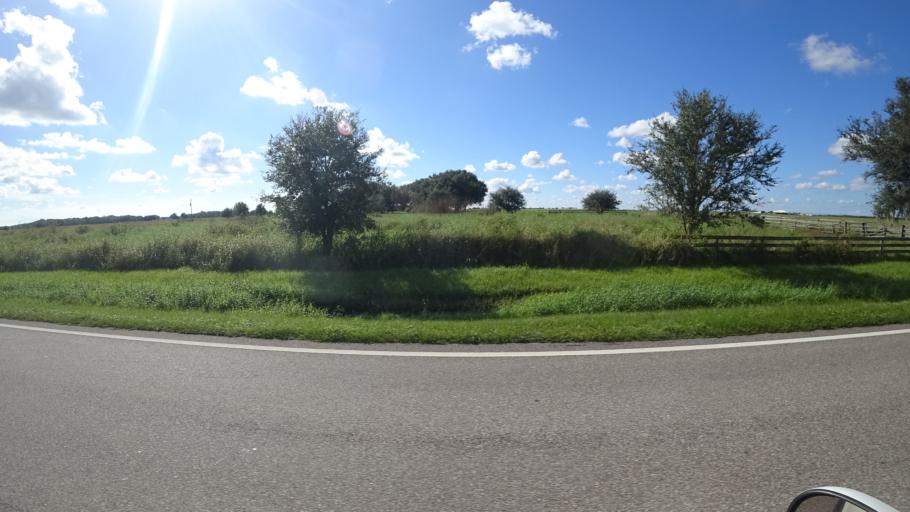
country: US
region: Florida
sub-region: Sarasota County
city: Lake Sarasota
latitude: 27.3621
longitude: -82.2684
